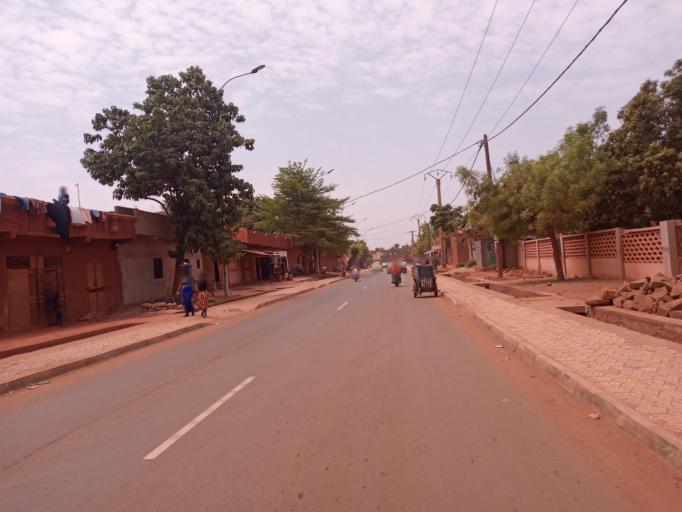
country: ML
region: Bamako
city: Bamako
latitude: 12.5813
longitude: -7.9882
